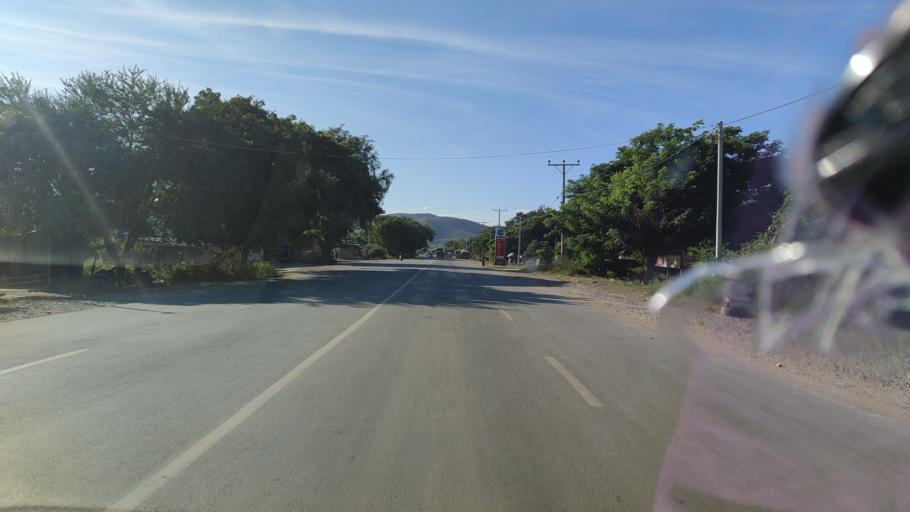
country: MM
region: Mandalay
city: Yamethin
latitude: 20.7537
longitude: 96.2568
